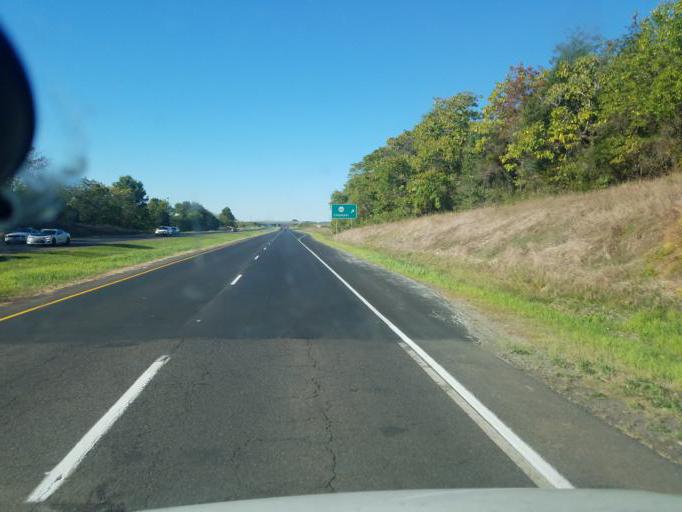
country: US
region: Virginia
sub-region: Culpeper County
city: Culpeper
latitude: 38.4788
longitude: -77.9464
